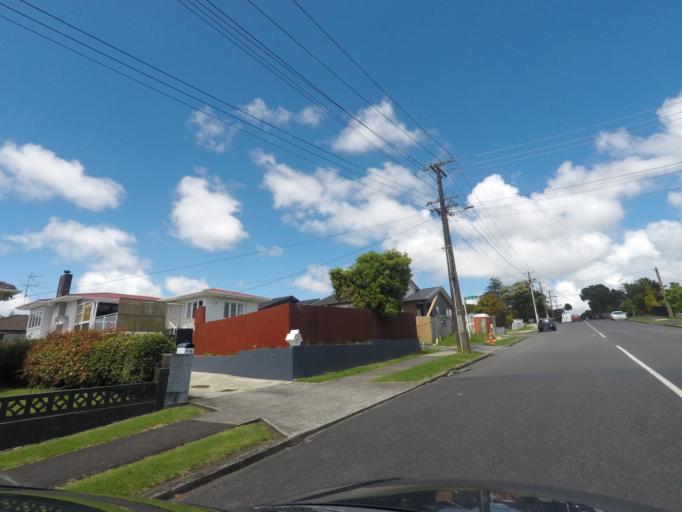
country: NZ
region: Auckland
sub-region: Auckland
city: Rosebank
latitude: -36.8774
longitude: 174.6428
